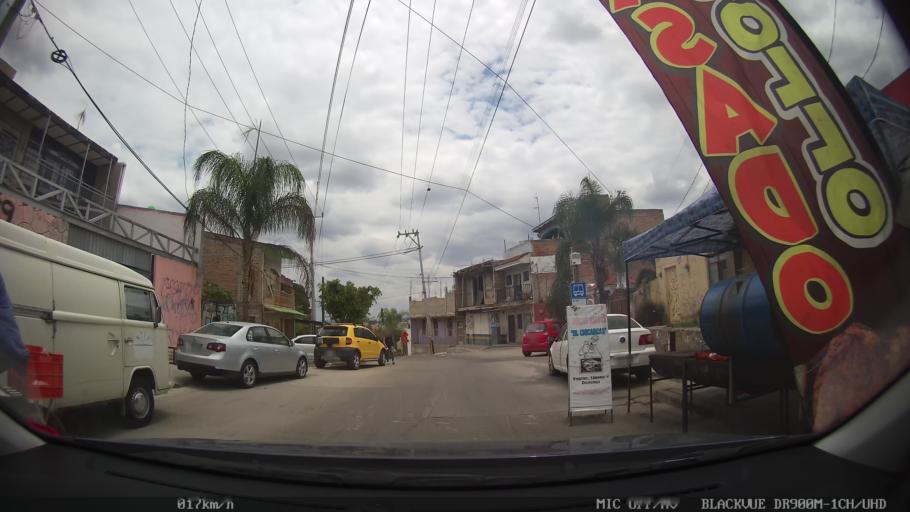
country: MX
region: Jalisco
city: Tlaquepaque
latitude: 20.6455
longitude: -103.2612
